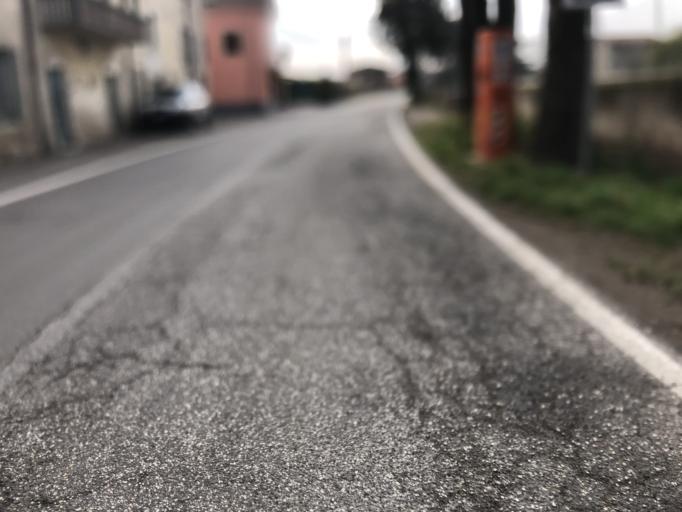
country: IT
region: Veneto
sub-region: Provincia di Verona
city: Sona
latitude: 45.4255
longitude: 10.8237
